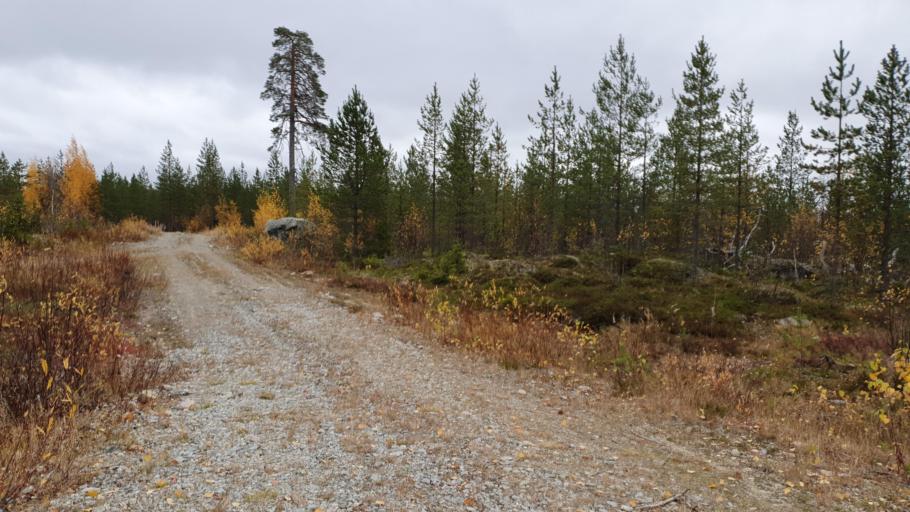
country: FI
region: Kainuu
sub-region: Kehys-Kainuu
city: Kuhmo
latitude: 64.4513
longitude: 29.5884
